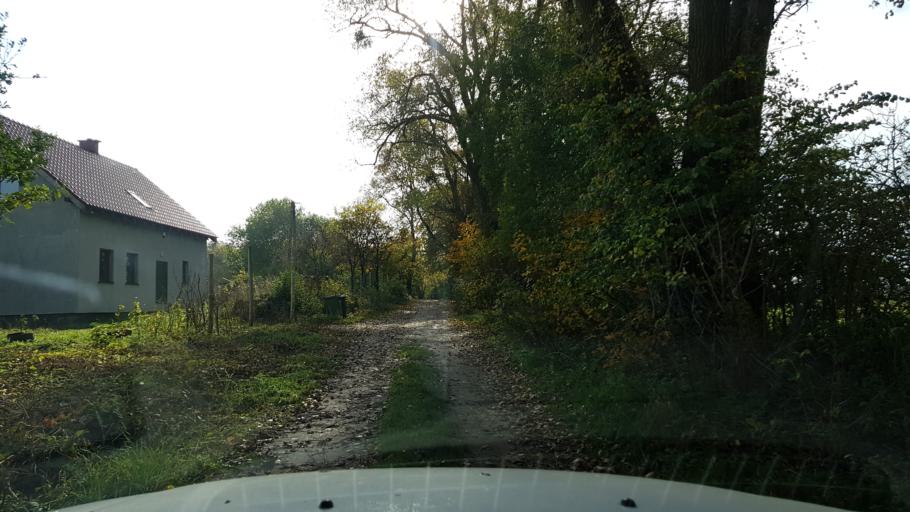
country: PL
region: West Pomeranian Voivodeship
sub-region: Powiat swidwinski
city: Polczyn-Zdroj
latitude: 53.7619
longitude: 16.0289
